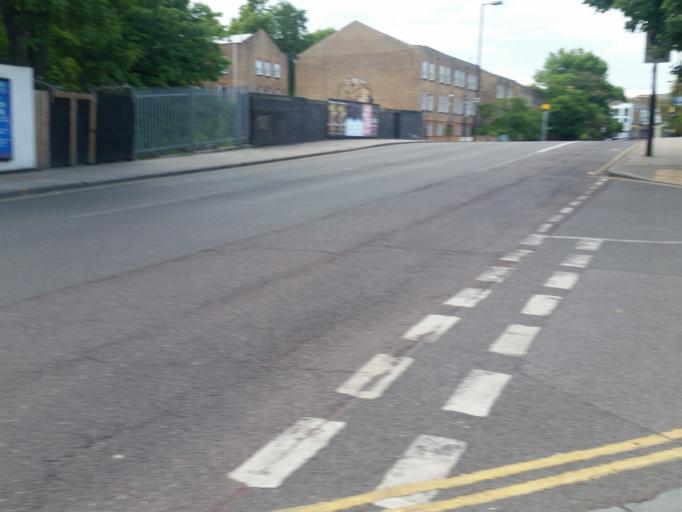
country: GB
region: England
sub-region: Greater London
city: Holloway
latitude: 51.5584
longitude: -0.1377
